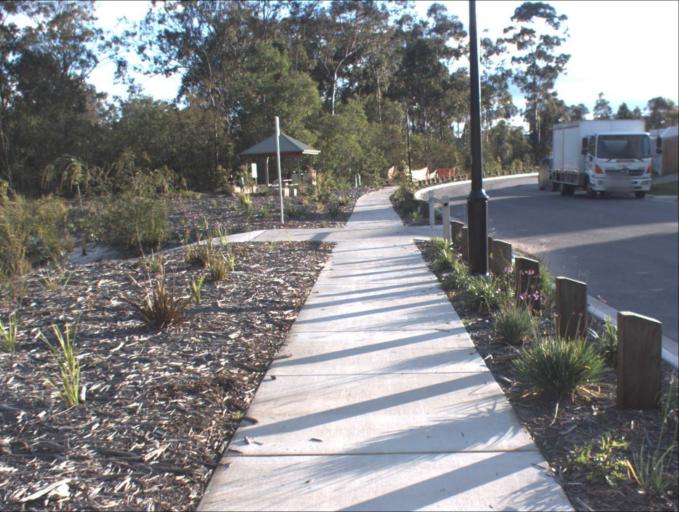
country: AU
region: Queensland
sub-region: Logan
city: North Maclean
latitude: -27.8041
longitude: 152.9620
